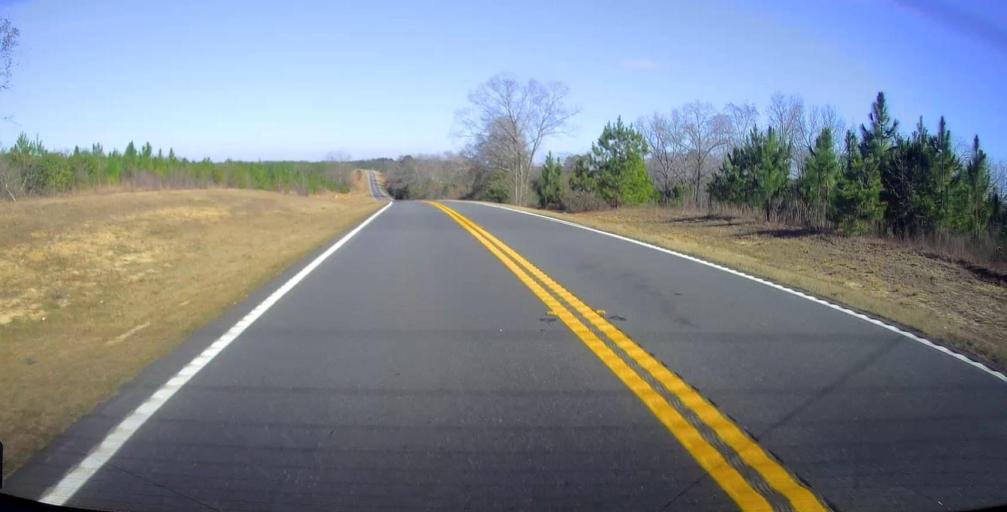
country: US
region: Georgia
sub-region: Taylor County
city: Butler
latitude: 32.4399
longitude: -84.2723
